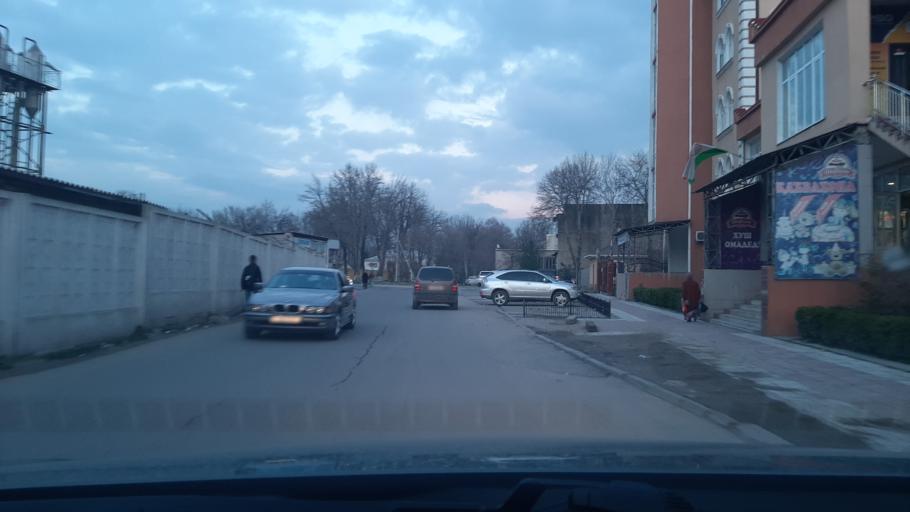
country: TJ
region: Dushanbe
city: Dushanbe
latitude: 38.5701
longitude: 68.7596
